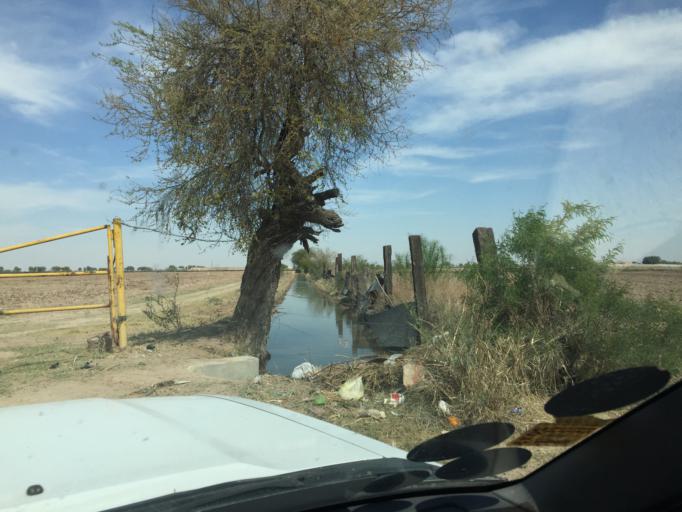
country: MX
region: Durango
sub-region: Gomez Palacio
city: El Vergel
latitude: 25.7260
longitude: -103.5249
